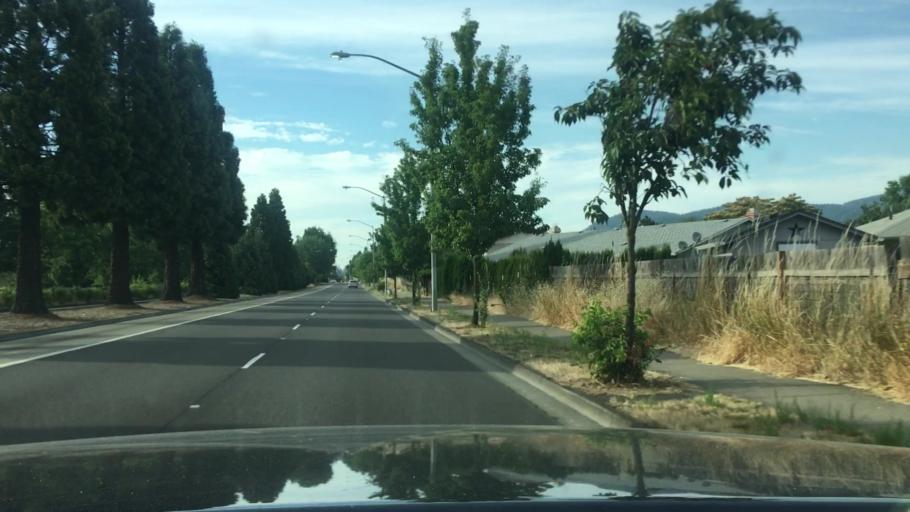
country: US
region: Oregon
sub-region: Lane County
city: Springfield
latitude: 44.0659
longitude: -123.0270
